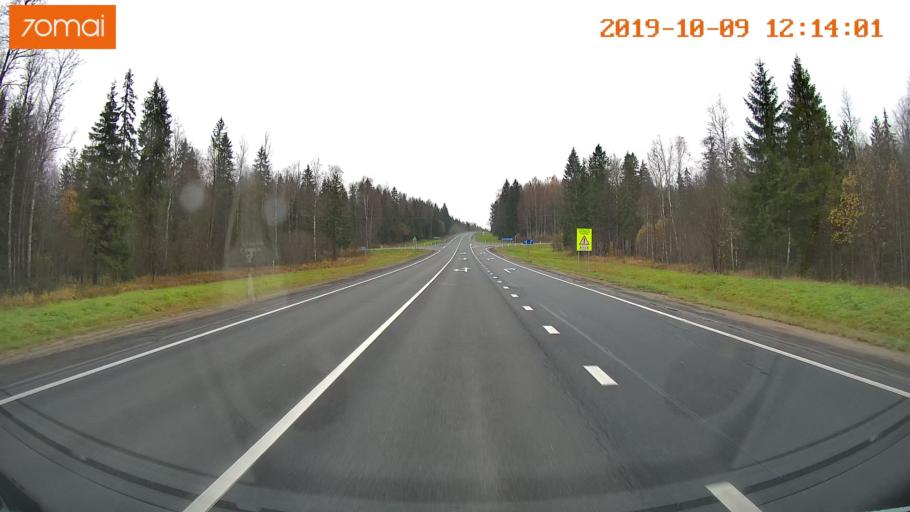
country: RU
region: Jaroslavl
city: Prechistoye
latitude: 58.5017
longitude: 40.3417
